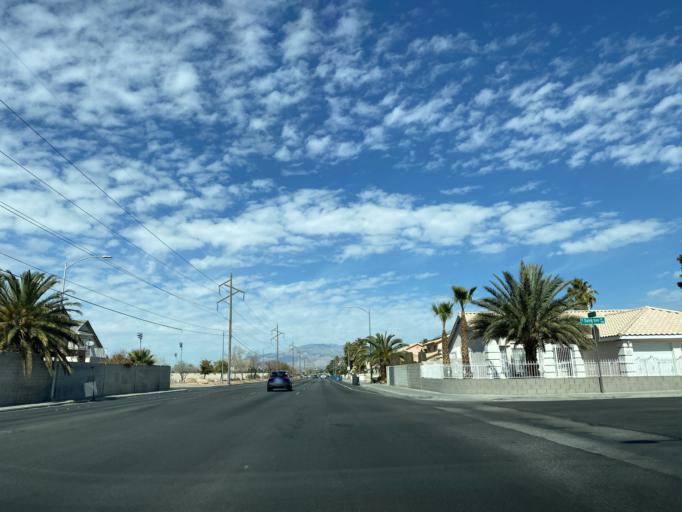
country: US
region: Nevada
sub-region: Clark County
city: Spring Valley
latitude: 36.2211
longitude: -115.2513
